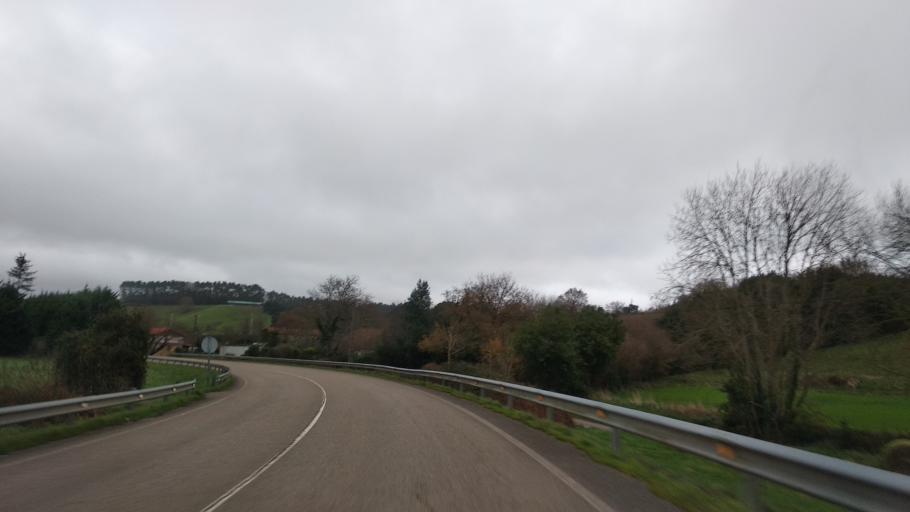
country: ES
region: Cantabria
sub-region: Provincia de Cantabria
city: Entrambasaguas
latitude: 43.4044
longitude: -3.7194
